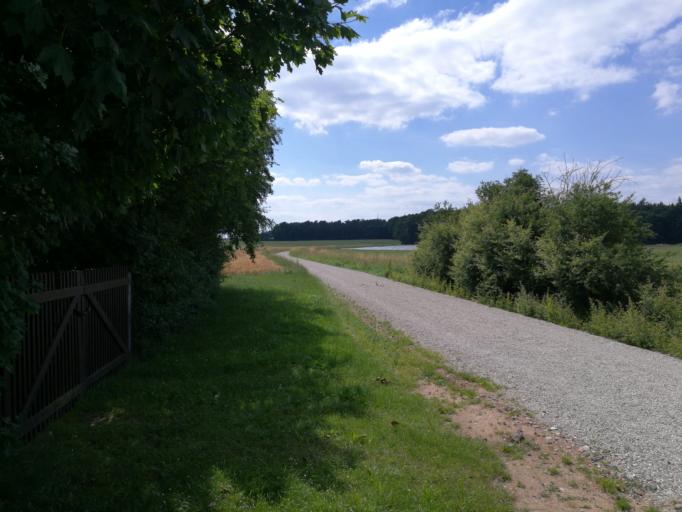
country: DE
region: Bavaria
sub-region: Regierungsbezirk Mittelfranken
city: Seukendorf
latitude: 49.4937
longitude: 10.9040
